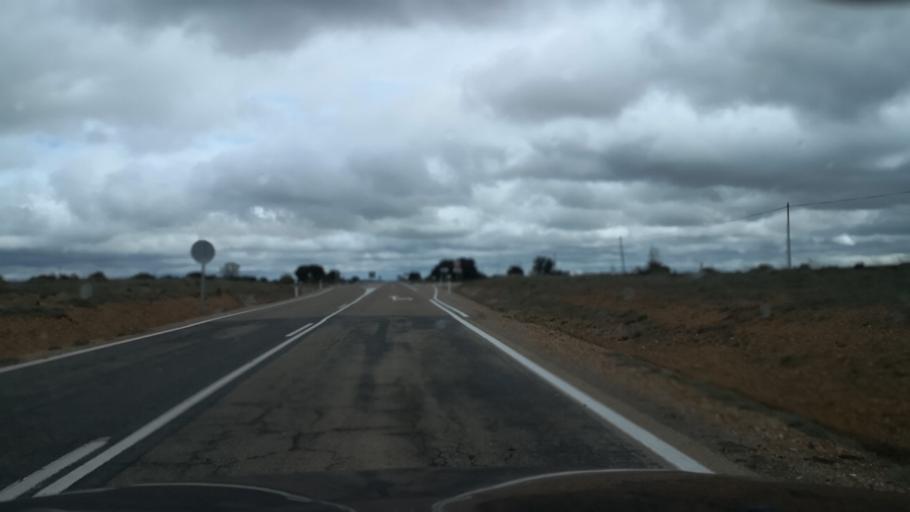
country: ES
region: Castille and Leon
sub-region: Provincia de Zamora
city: Perilla de Castro
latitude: 41.7365
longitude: -5.8288
